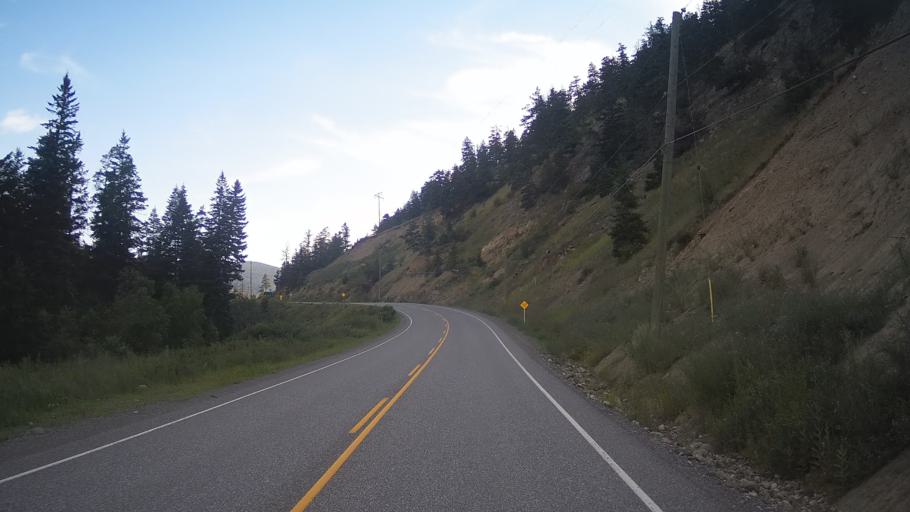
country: CA
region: British Columbia
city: Cache Creek
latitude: 50.8668
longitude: -121.5255
